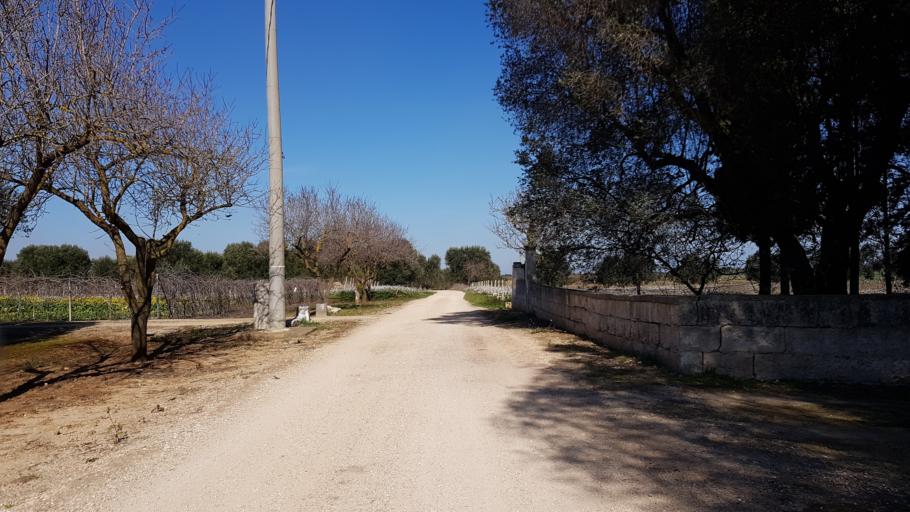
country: IT
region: Apulia
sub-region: Provincia di Brindisi
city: Mesagne
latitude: 40.6168
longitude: 17.8045
